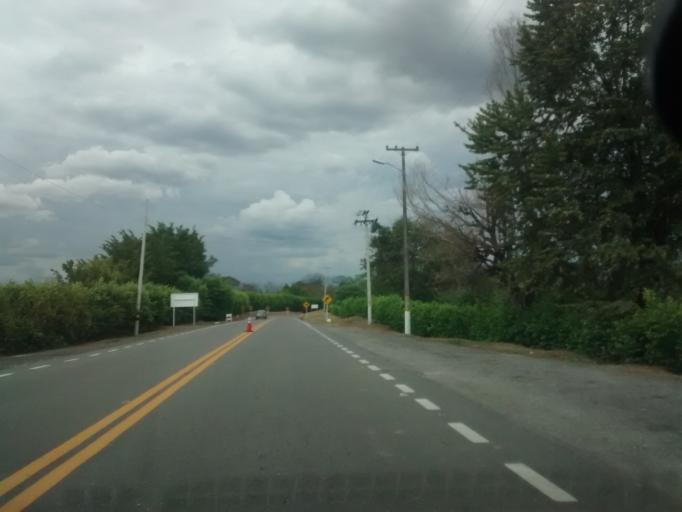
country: CO
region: Cundinamarca
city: Agua de Dios
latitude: 4.4092
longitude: -74.7152
